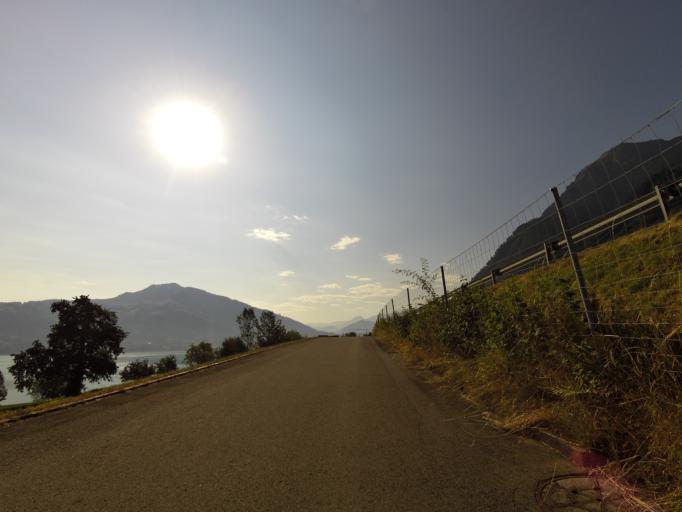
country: CH
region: Schwyz
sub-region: Bezirk Kuessnacht
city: Kussnacht
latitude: 47.0854
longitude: 8.4756
